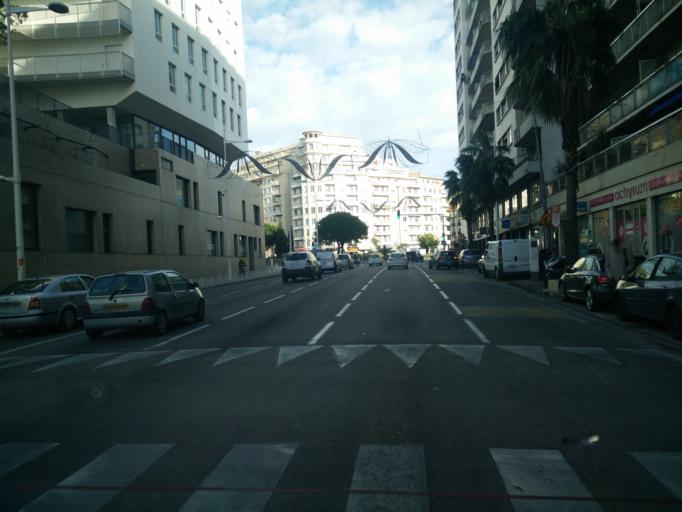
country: FR
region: Provence-Alpes-Cote d'Azur
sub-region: Departement du Var
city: Toulon
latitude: 43.1206
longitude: 5.9400
